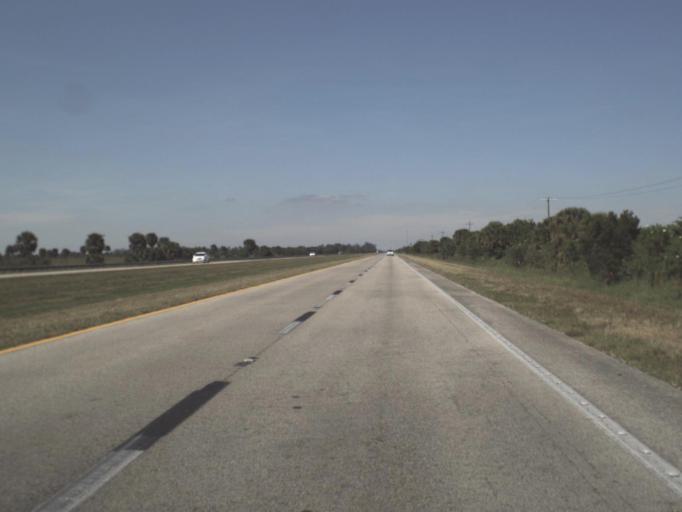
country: US
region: Florida
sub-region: Glades County
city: Moore Haven
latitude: 26.8412
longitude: -81.1962
